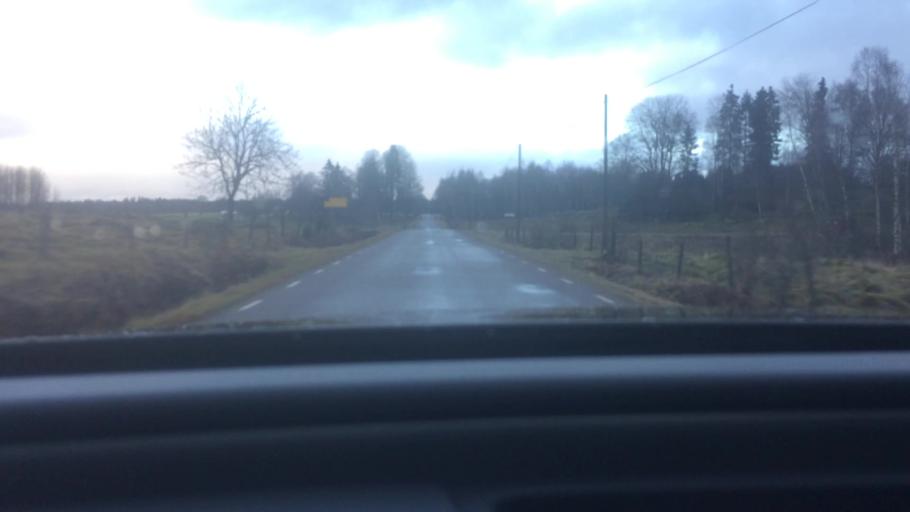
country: SE
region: Vaestra Goetaland
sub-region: Falkopings Kommun
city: Falkoeping
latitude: 58.0115
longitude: 13.5008
